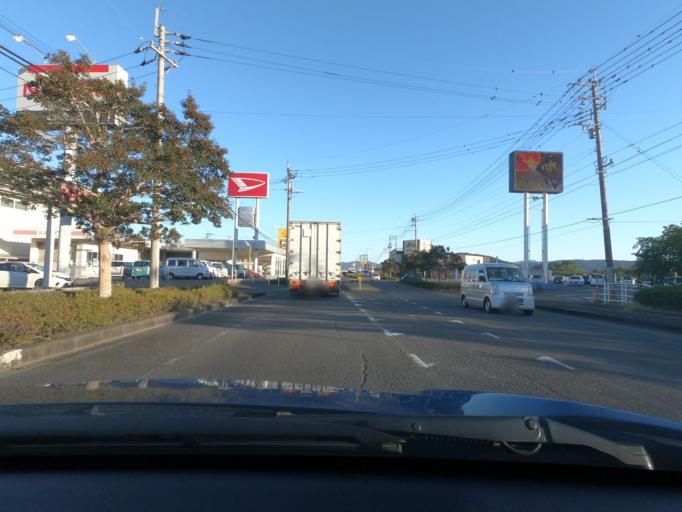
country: JP
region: Kagoshima
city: Satsumasendai
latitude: 31.8379
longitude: 130.2850
